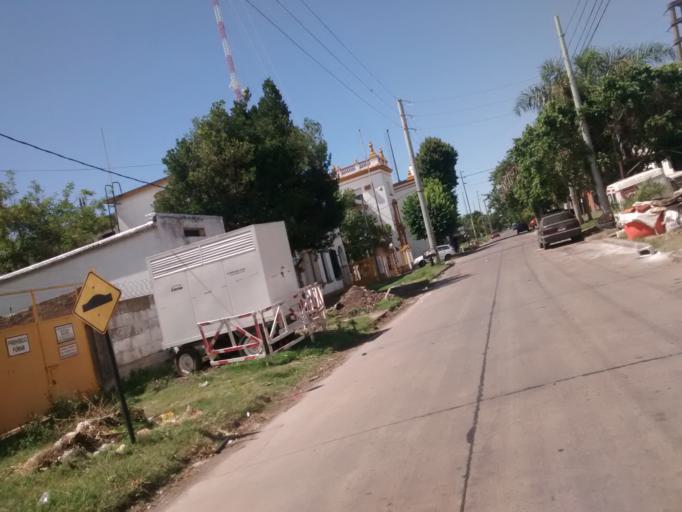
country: AR
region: Buenos Aires
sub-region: Partido de La Plata
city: La Plata
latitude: -34.9445
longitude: -57.9757
